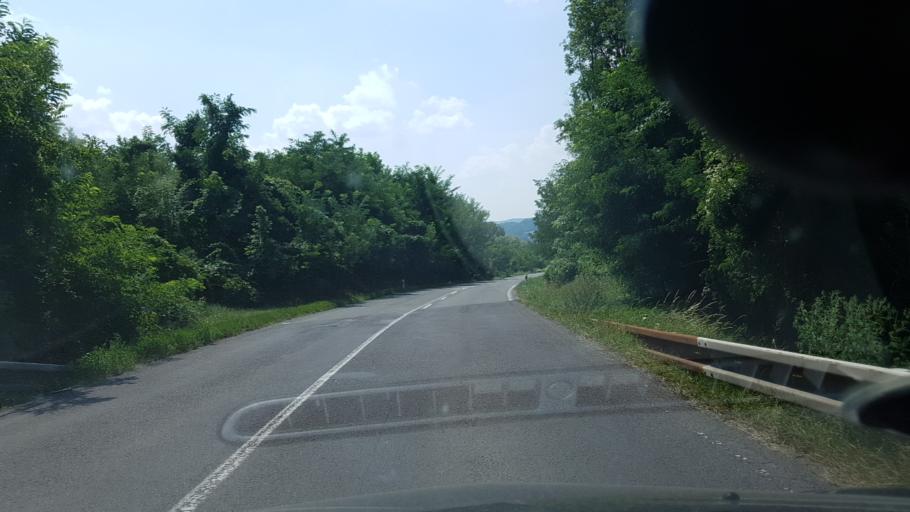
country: SK
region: Banskobystricky
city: Velky Krtis
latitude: 48.2447
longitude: 19.4307
